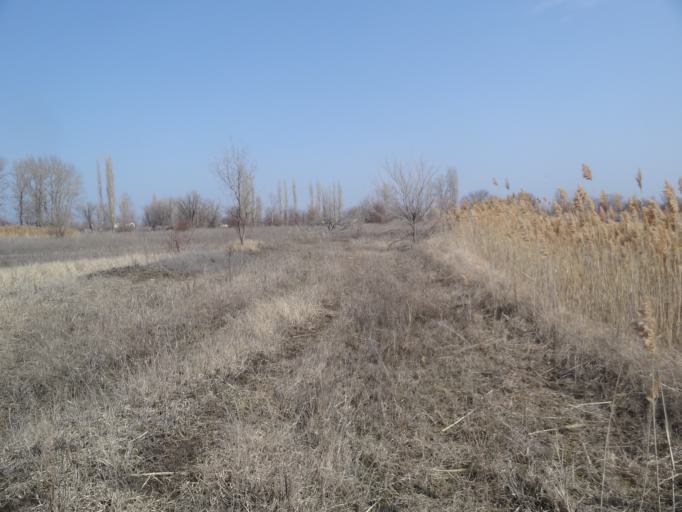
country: RU
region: Saratov
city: Engel's
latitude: 51.4344
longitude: 46.2218
